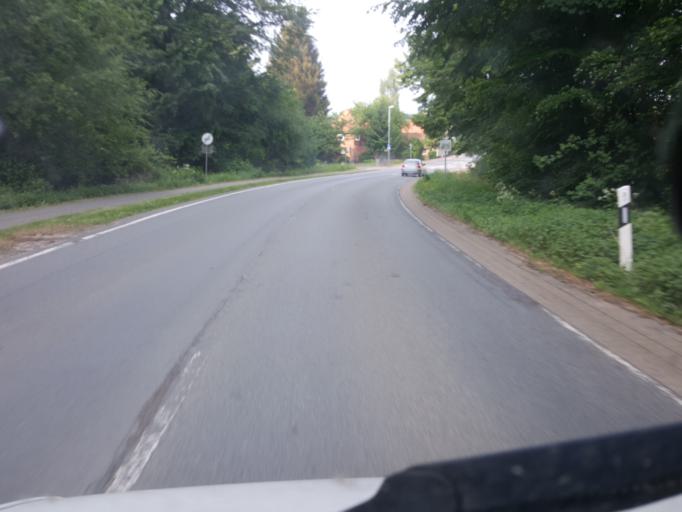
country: DE
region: Lower Saxony
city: Binnen
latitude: 52.6409
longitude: 9.1381
